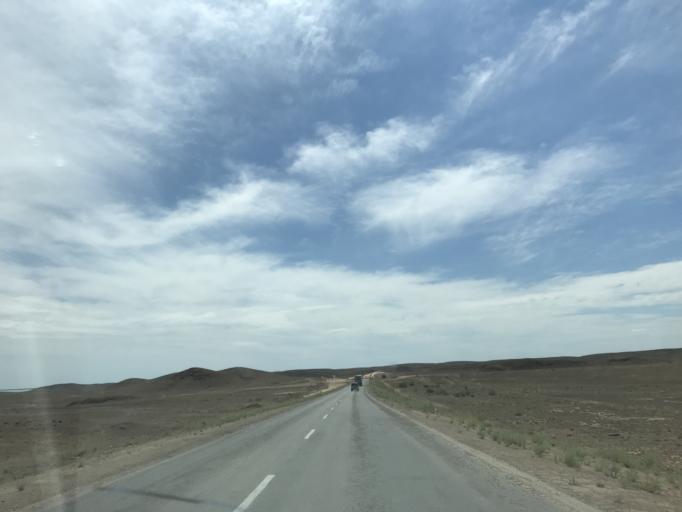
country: KZ
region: Almaty Oblysy
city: Ulken
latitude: 45.0722
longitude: 73.9894
